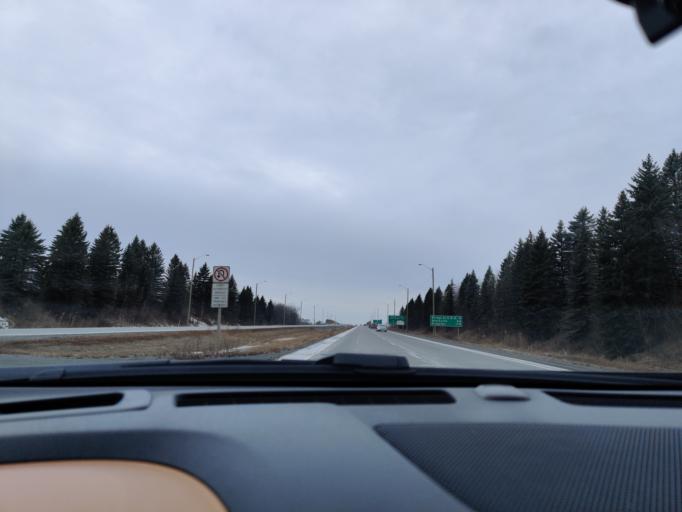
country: CA
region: Ontario
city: Cornwall
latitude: 45.0523
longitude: -74.7469
